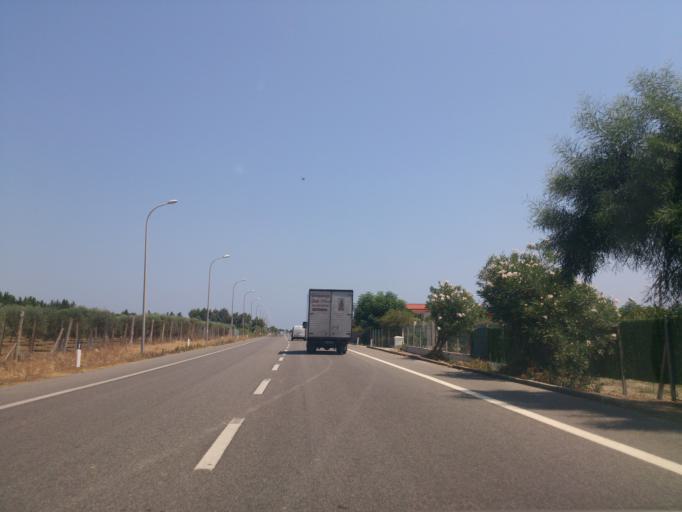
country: IT
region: Calabria
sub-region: Provincia di Reggio Calabria
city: Monasterace Marina
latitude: 38.4140
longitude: 16.5573
